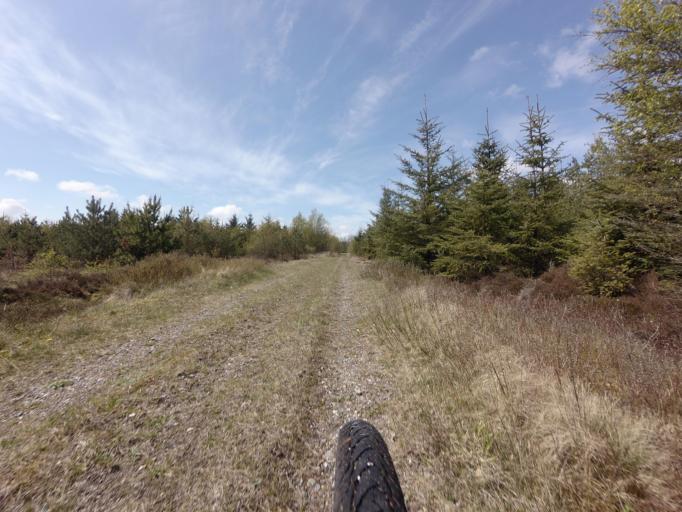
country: DK
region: North Denmark
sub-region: Jammerbugt Kommune
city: Brovst
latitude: 57.1648
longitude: 9.5455
